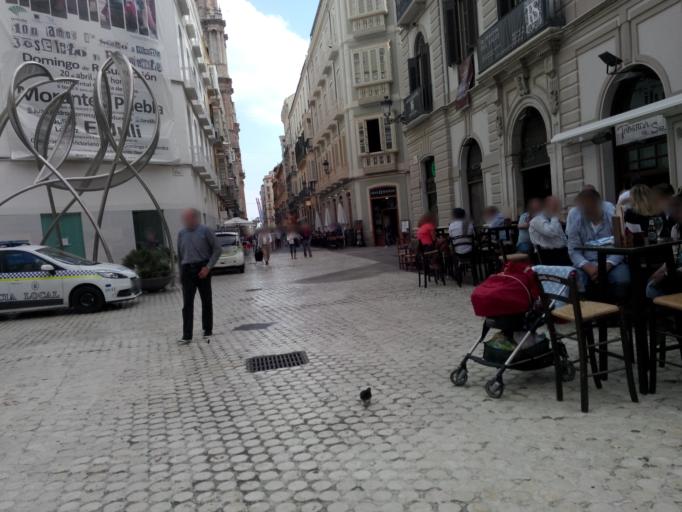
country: ES
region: Andalusia
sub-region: Provincia de Malaga
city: Malaga
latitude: 36.7217
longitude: -4.4202
